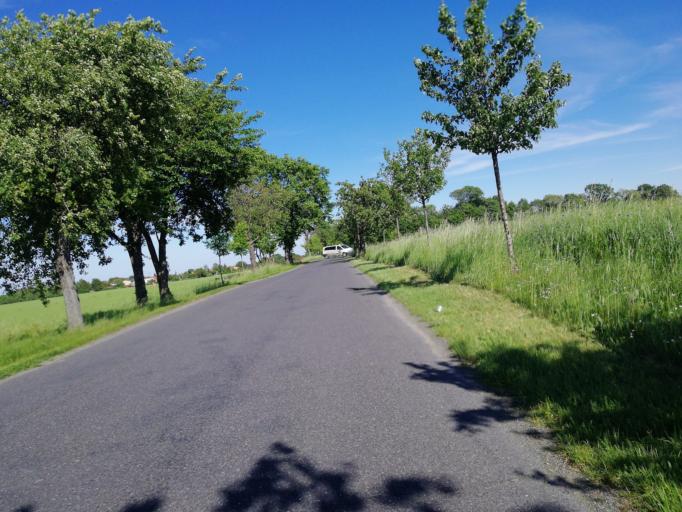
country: DE
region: Brandenburg
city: Calau
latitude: 51.7462
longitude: 13.9335
